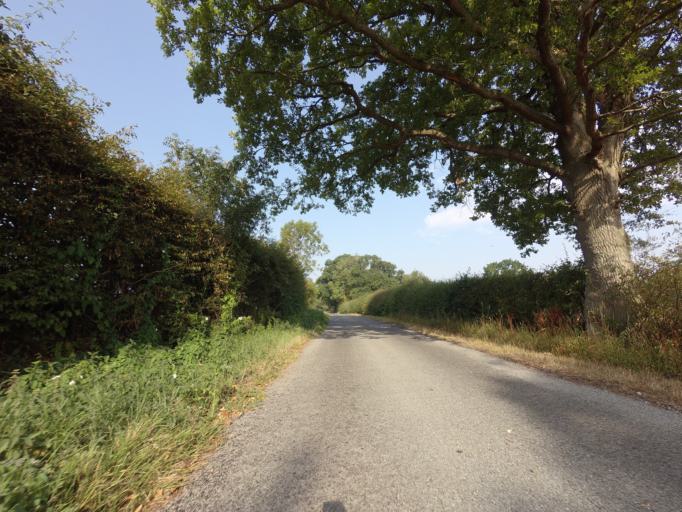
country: GB
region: England
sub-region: Kent
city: Headcorn
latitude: 51.1285
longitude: 0.6568
